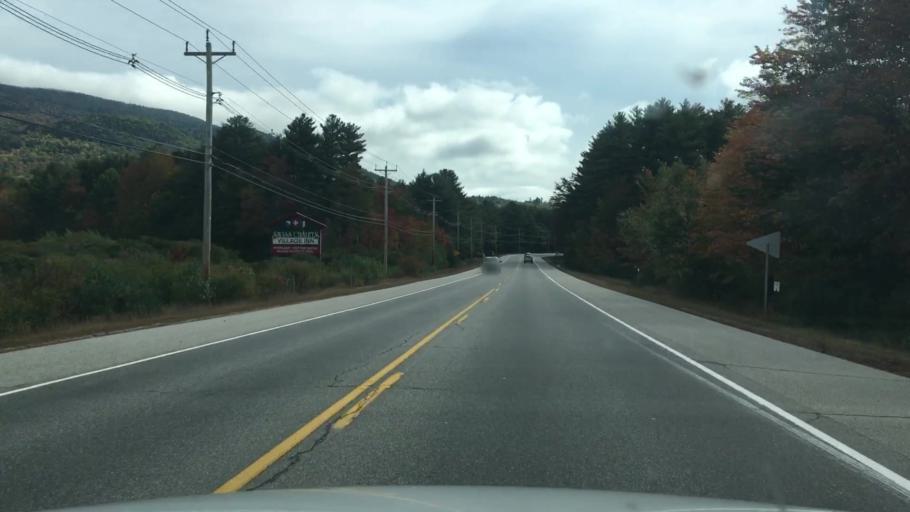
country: US
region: New Hampshire
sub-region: Carroll County
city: North Conway
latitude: 44.1053
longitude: -71.1570
